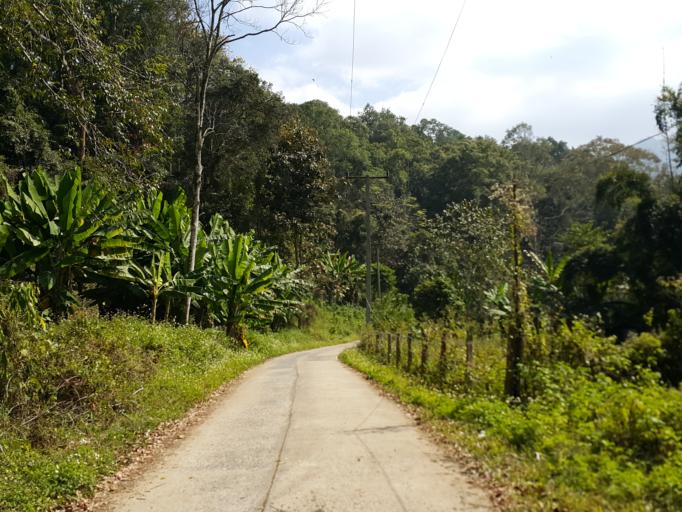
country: TH
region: Lampang
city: Wang Nuea
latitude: 19.0635
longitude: 99.3609
